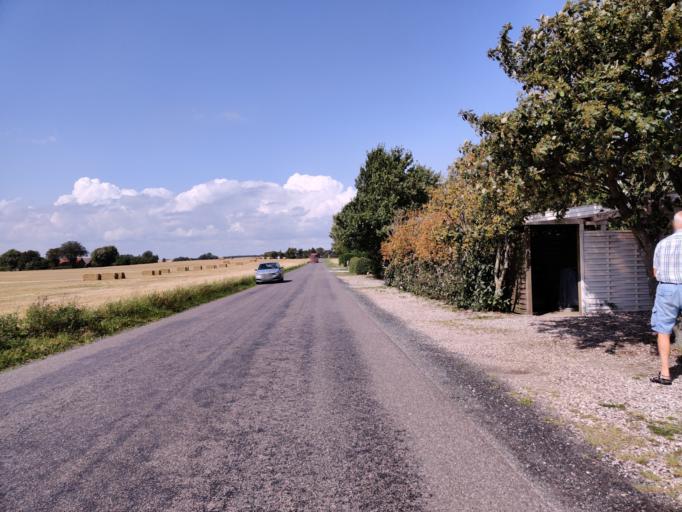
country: DK
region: Zealand
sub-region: Guldborgsund Kommune
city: Nykobing Falster
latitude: 54.6177
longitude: 11.9153
